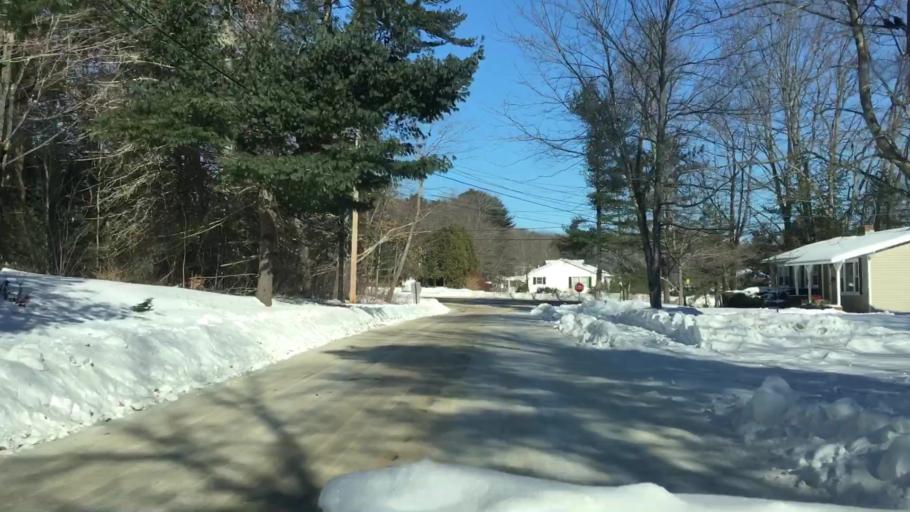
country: US
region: Maine
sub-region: Sagadahoc County
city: Topsham
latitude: 43.9256
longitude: -69.9719
